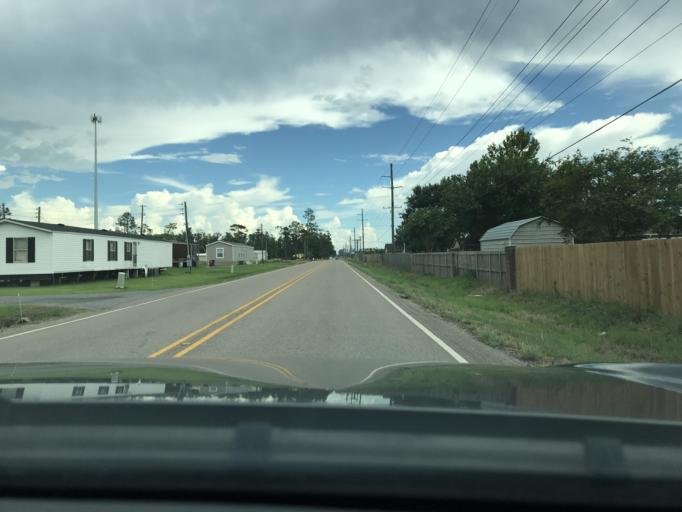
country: US
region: Louisiana
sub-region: Calcasieu Parish
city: Moss Bluff
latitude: 30.3396
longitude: -93.2329
